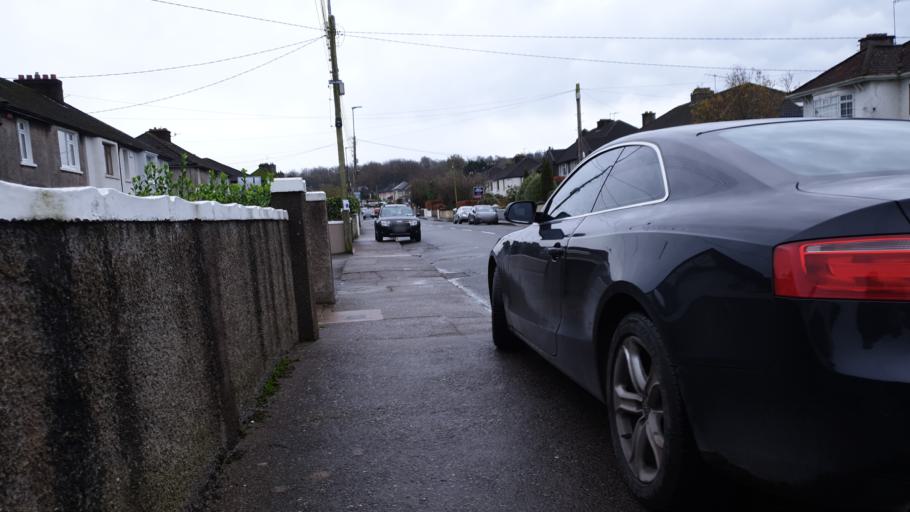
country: IE
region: Munster
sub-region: County Cork
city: Cork
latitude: 51.8954
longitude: -8.4309
